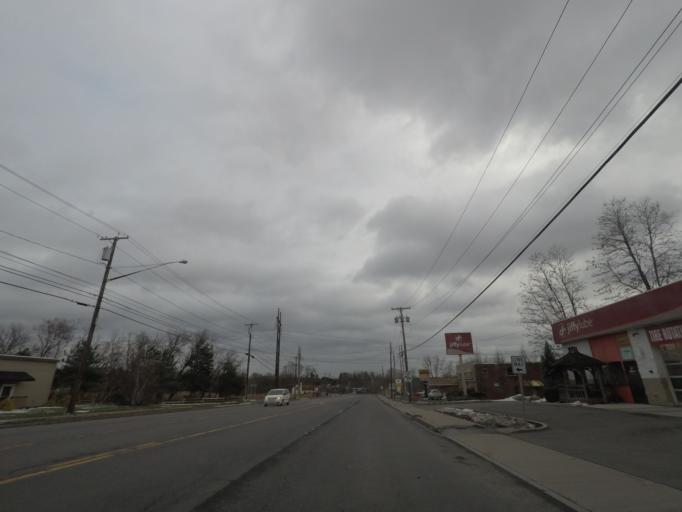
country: US
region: New York
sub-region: Rensselaer County
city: Hampton Manor
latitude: 42.6102
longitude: -73.7261
